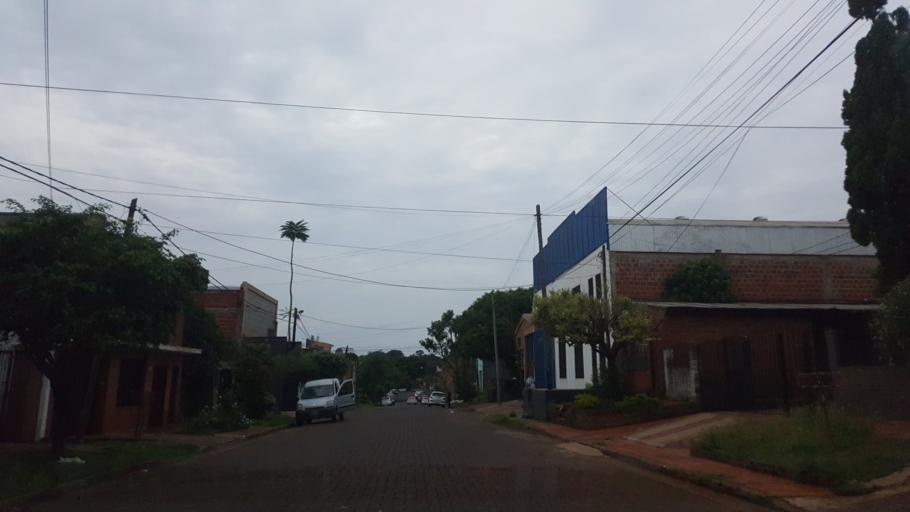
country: AR
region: Misiones
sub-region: Departamento de Capital
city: Posadas
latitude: -27.4033
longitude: -55.9050
